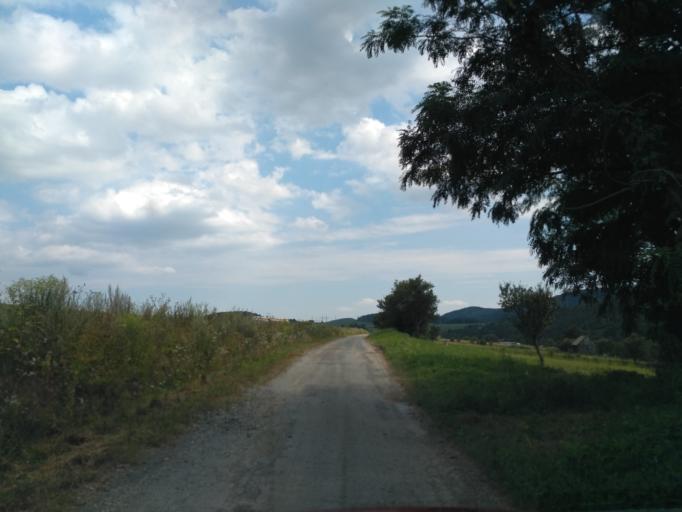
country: SK
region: Presovsky
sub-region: Okres Presov
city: Presov
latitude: 48.9144
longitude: 21.1752
